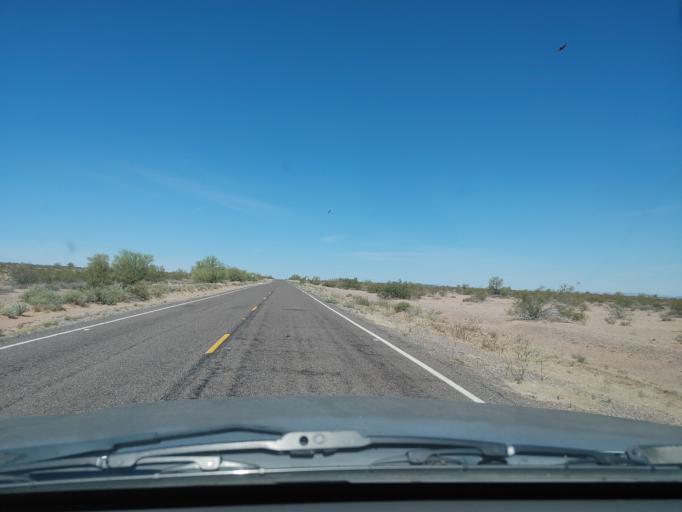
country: US
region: Arizona
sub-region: Maricopa County
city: Gila Bend
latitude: 32.8806
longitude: -113.2262
